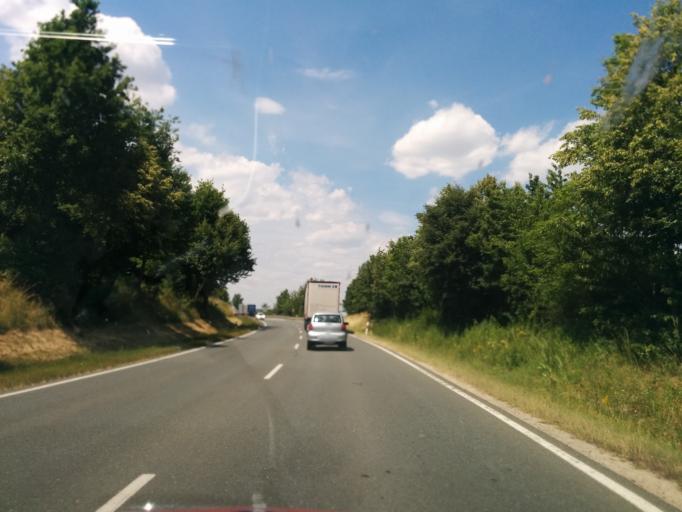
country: DE
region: Bavaria
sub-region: Regierungsbezirk Mittelfranken
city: Weissenburg in Bayern
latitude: 49.0366
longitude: 10.9870
